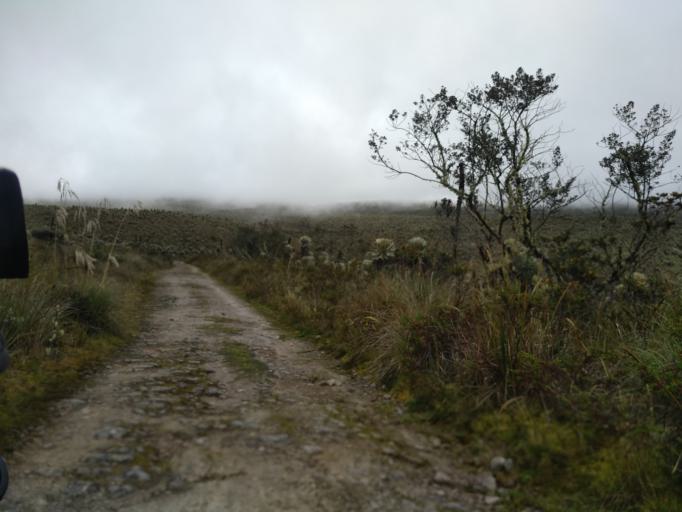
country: EC
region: Carchi
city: San Gabriel
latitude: 0.6852
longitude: -77.8511
